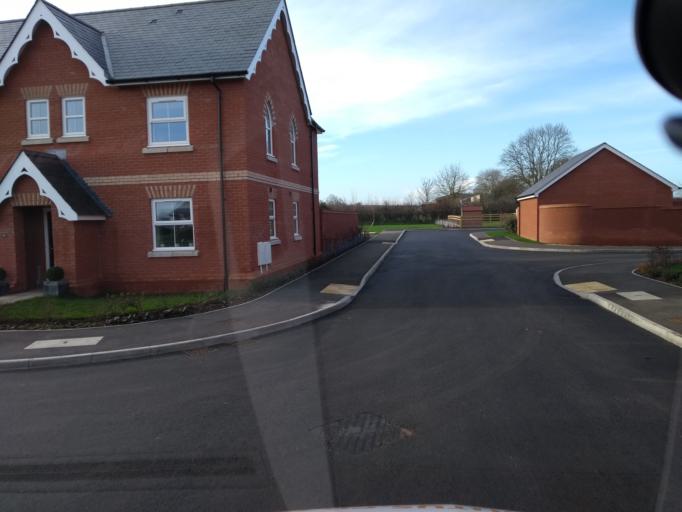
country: GB
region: England
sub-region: Somerset
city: Creech Saint Michael
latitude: 51.0231
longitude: -2.9757
